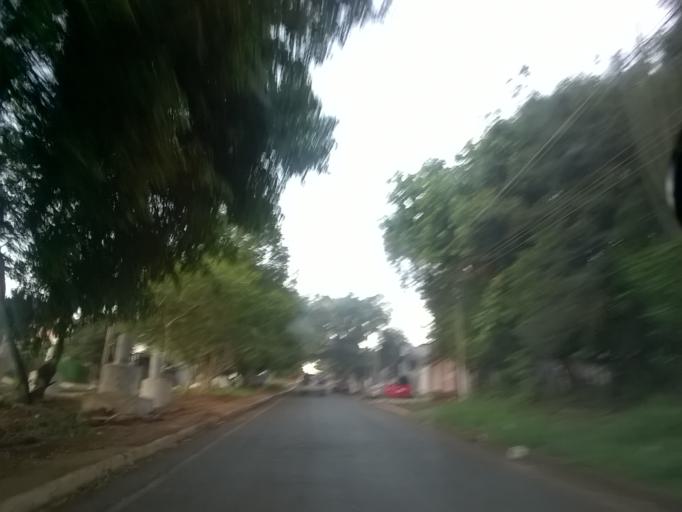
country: PY
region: Alto Parana
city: Ciudad del Este
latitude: -25.4922
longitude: -54.6487
